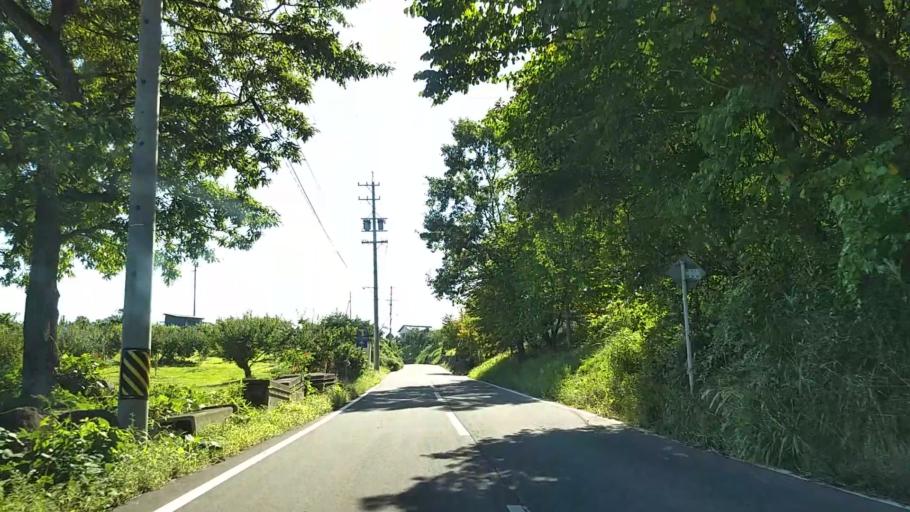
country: JP
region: Nagano
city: Nagano-shi
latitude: 36.5797
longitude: 138.1202
